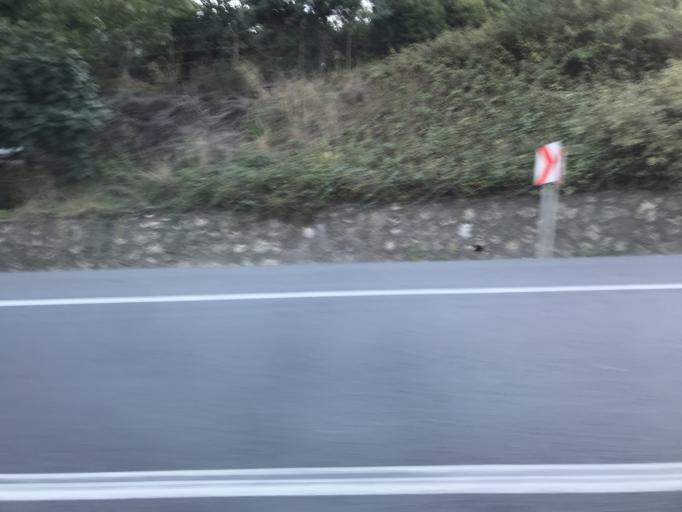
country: TR
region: Kocaeli
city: Darica
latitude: 40.7798
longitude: 29.4168
